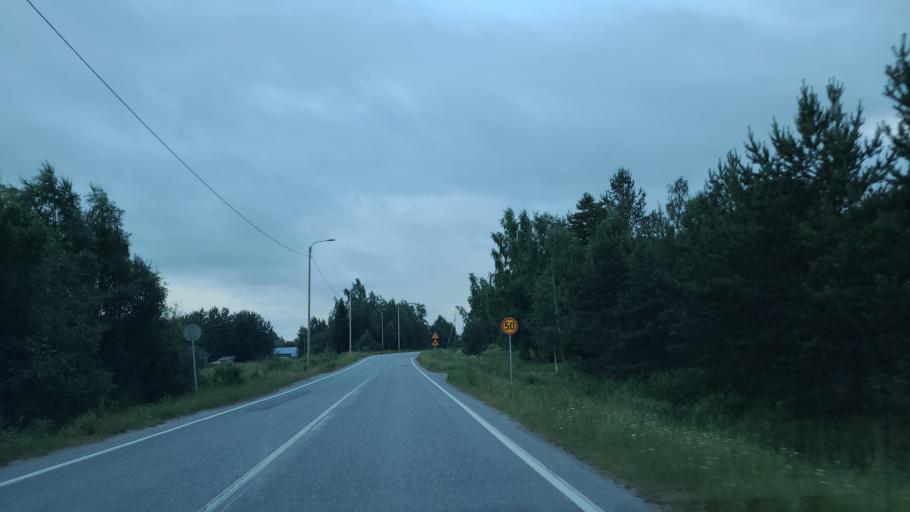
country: FI
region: Ostrobothnia
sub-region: Vaasa
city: Replot
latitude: 63.1996
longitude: 21.3035
